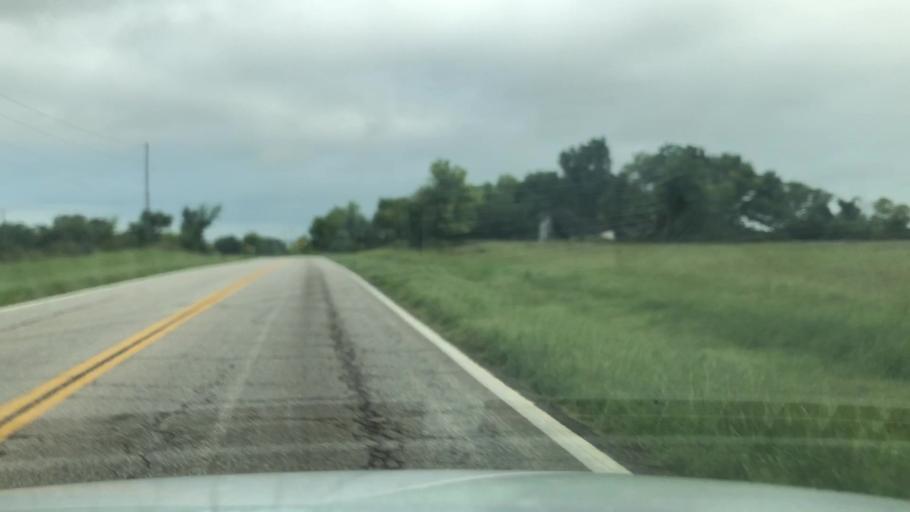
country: US
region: Oklahoma
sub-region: Nowata County
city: Nowata
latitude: 36.7124
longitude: -95.6619
